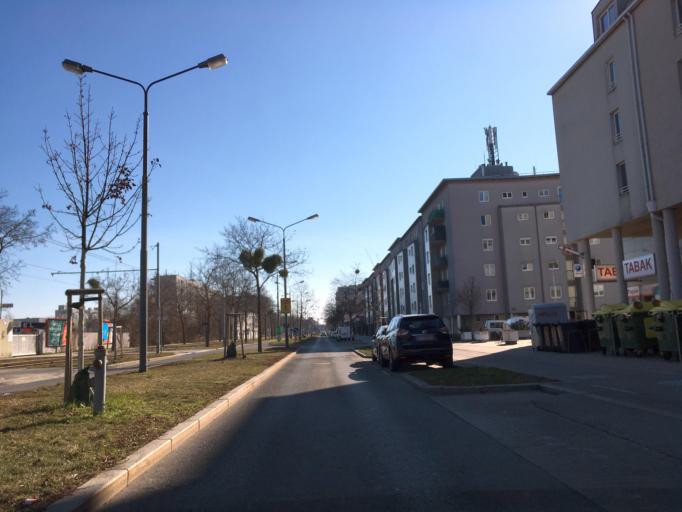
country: AT
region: Lower Austria
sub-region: Politischer Bezirk Wien-Umgebung
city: Gerasdorf bei Wien
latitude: 48.2183
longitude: 16.4726
